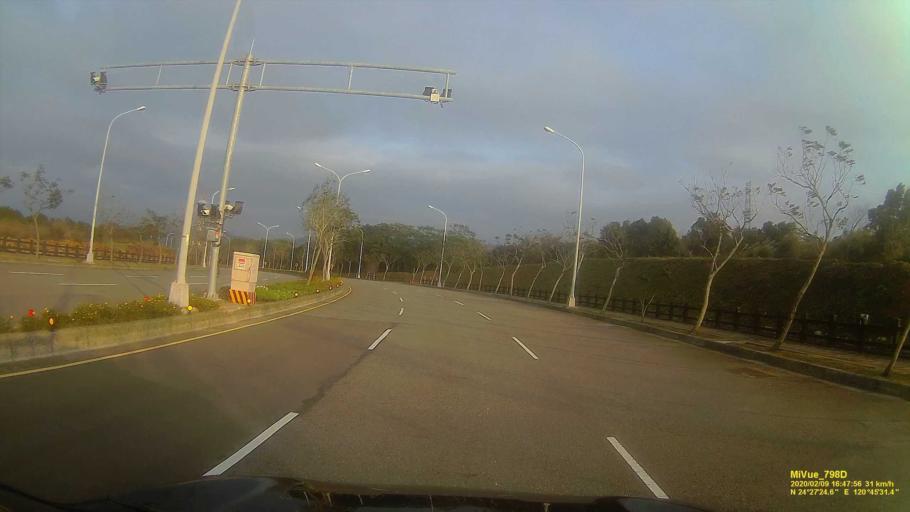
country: TW
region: Taiwan
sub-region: Miaoli
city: Miaoli
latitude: 24.4568
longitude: 120.7589
